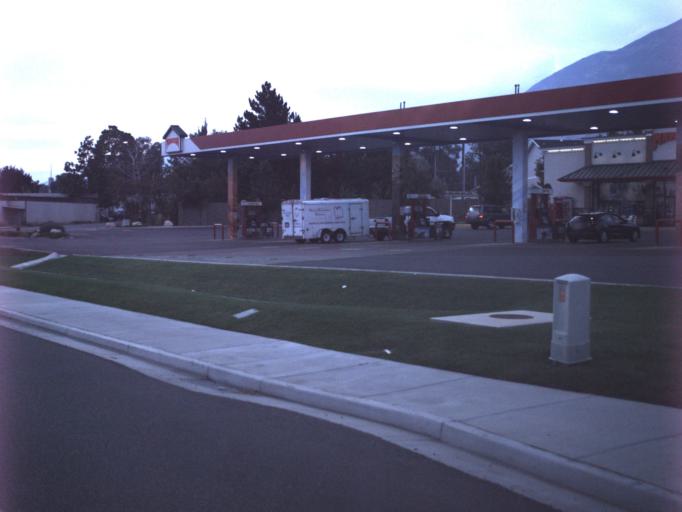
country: US
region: Utah
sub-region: Utah County
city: Pleasant Grove
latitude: 40.3551
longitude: -111.7353
